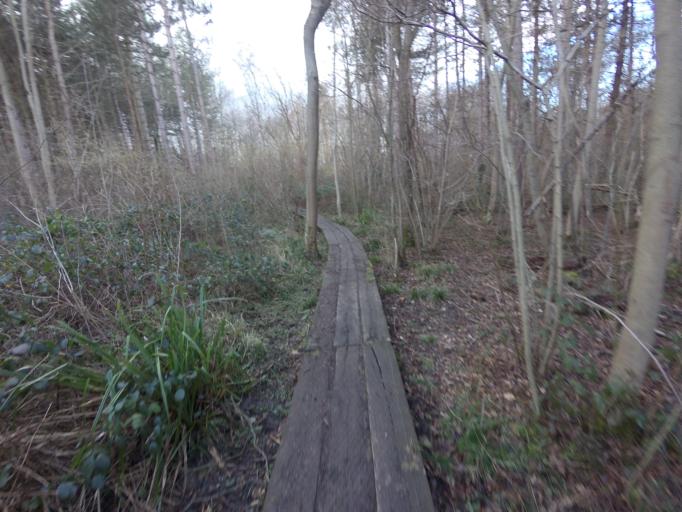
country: GB
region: England
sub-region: Greater London
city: Bexley
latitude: 51.4190
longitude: 0.1583
